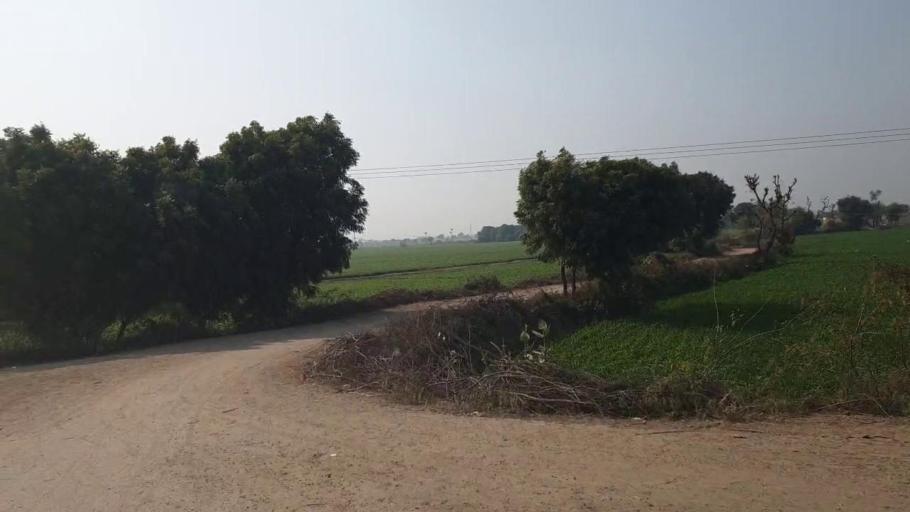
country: PK
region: Sindh
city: Hala
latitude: 25.8448
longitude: 68.4282
